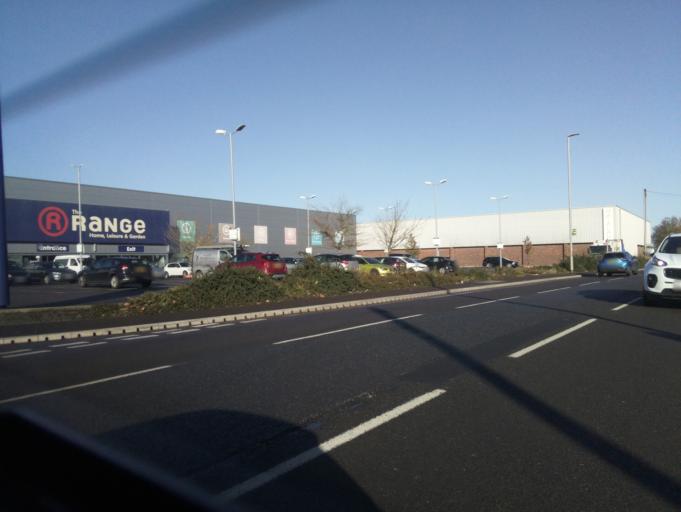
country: GB
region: England
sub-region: Somerset
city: Bridgwater
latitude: 51.1380
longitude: -2.9933
